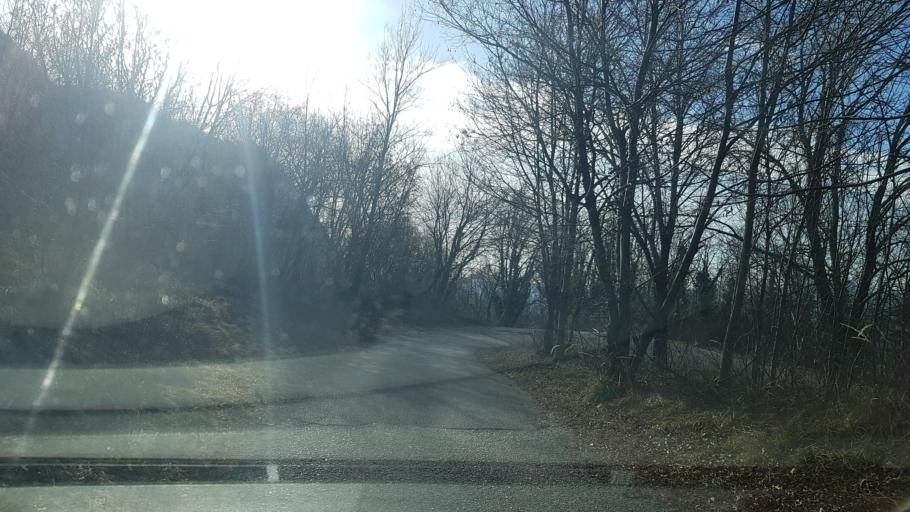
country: IT
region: Friuli Venezia Giulia
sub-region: Provincia di Udine
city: Gemona
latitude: 46.2852
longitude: 13.1472
